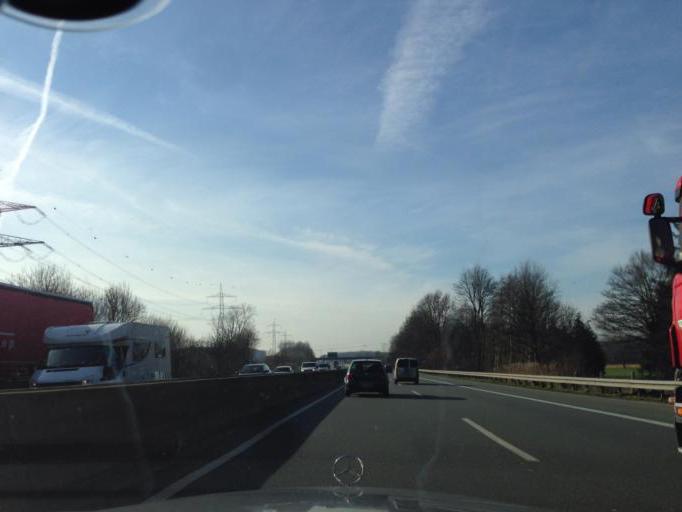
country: DE
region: North Rhine-Westphalia
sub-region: Regierungsbezirk Munster
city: Lotte
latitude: 52.2676
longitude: 7.9025
